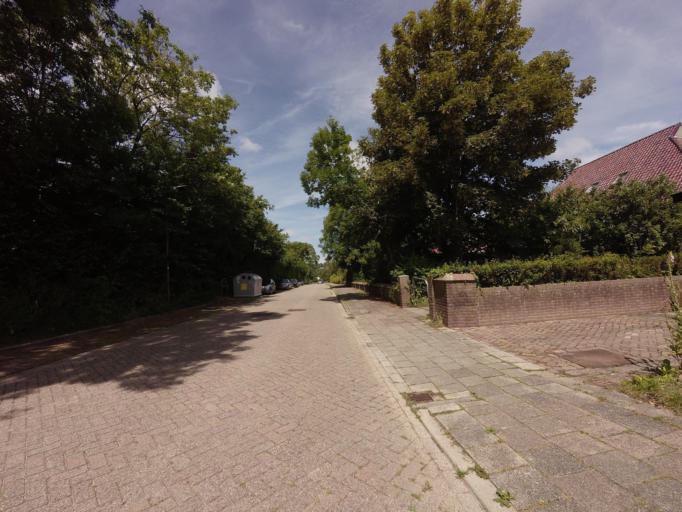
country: NL
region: North Holland
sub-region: Gemeente Texel
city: Den Burg
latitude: 53.0854
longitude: 4.8709
